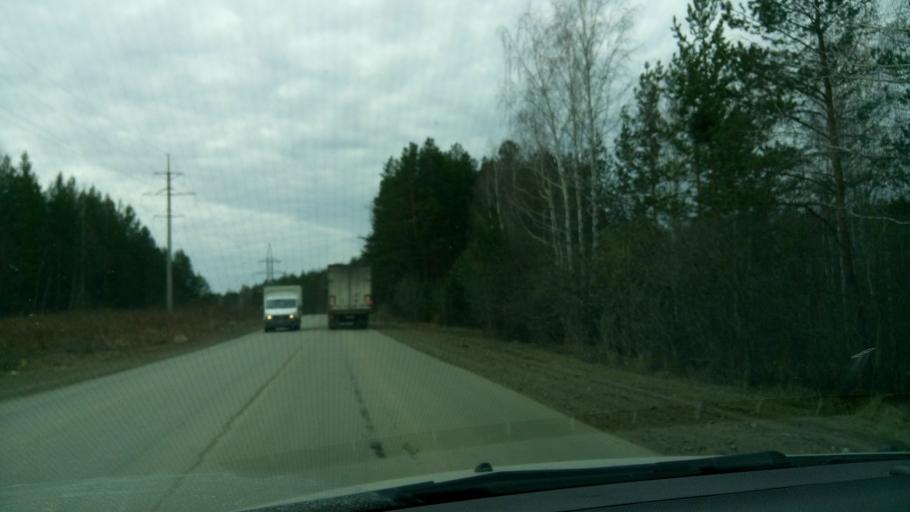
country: RU
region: Sverdlovsk
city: Verkhnyaya Pyshma
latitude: 56.9549
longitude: 60.6508
